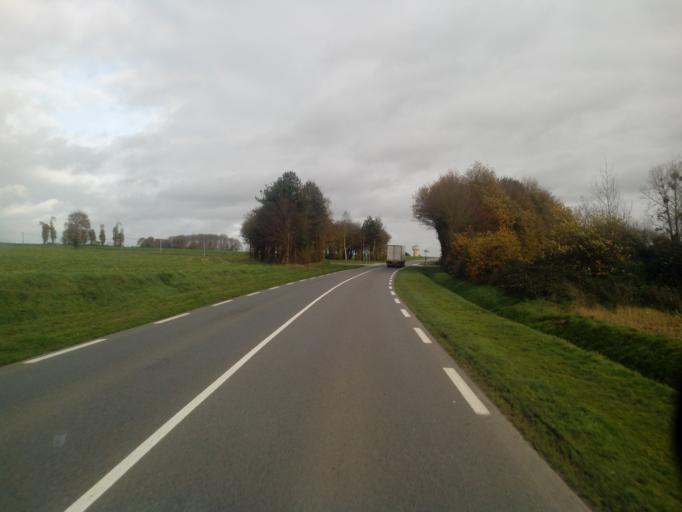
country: FR
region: Brittany
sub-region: Departement d'Ille-et-Vilaine
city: Gael
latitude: 48.1358
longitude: -2.2290
